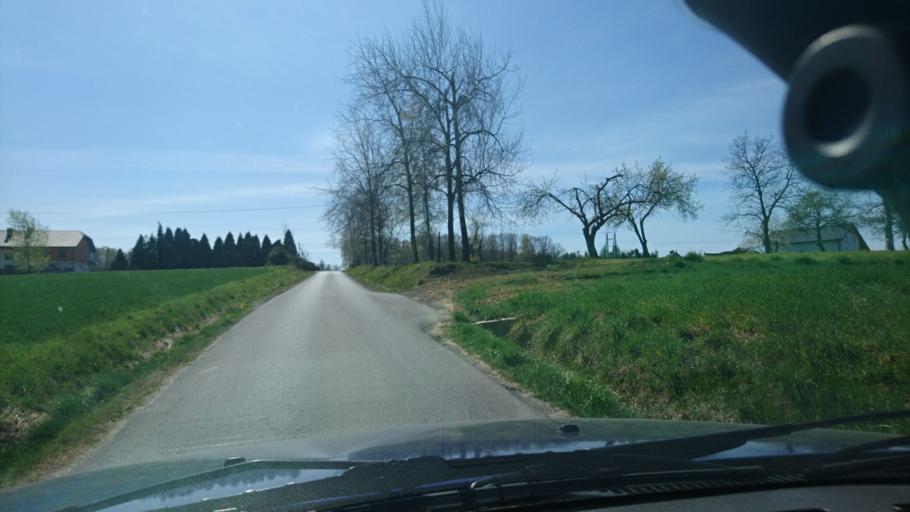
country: PL
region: Silesian Voivodeship
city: Janowice
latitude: 49.8900
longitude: 19.1036
